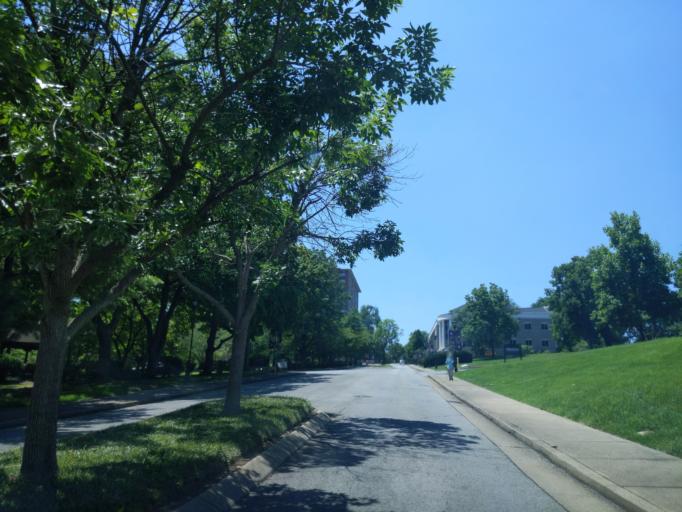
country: US
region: Tennessee
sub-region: Davidson County
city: Nashville
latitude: 36.1448
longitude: -86.7528
